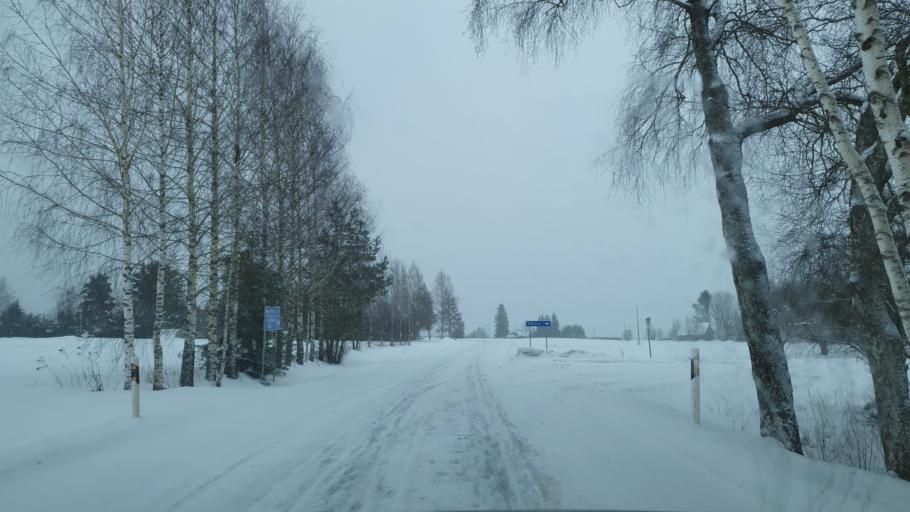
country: EE
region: Jogevamaa
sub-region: Tabivere vald
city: Tabivere
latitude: 58.5743
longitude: 26.7722
